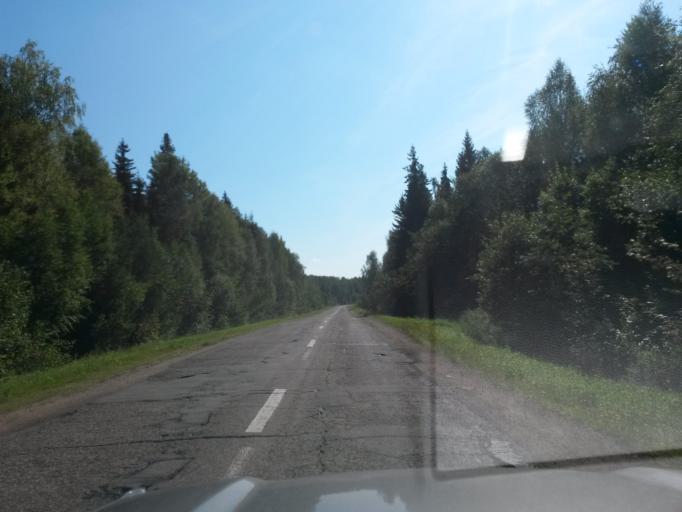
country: RU
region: Jaroslavl
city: Dubki
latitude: 57.2957
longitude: 40.0852
